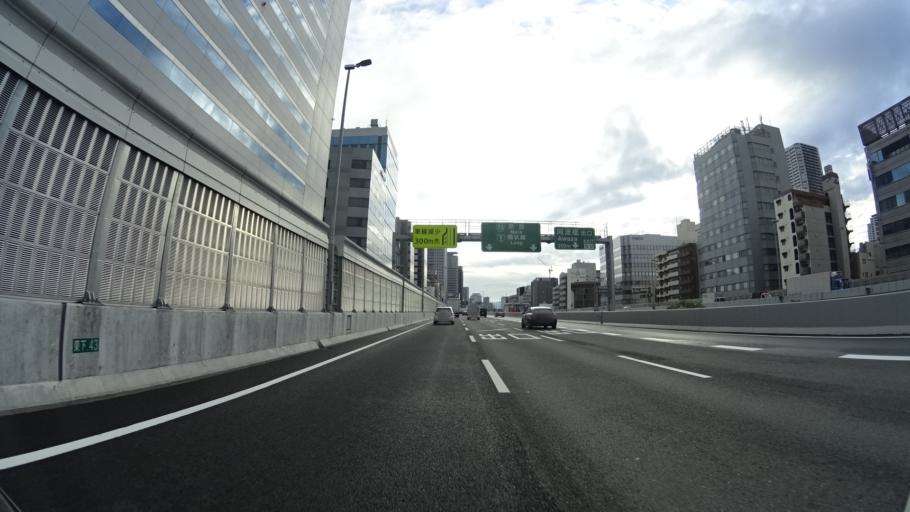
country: JP
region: Osaka
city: Osaka-shi
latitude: 34.6817
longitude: 135.4904
